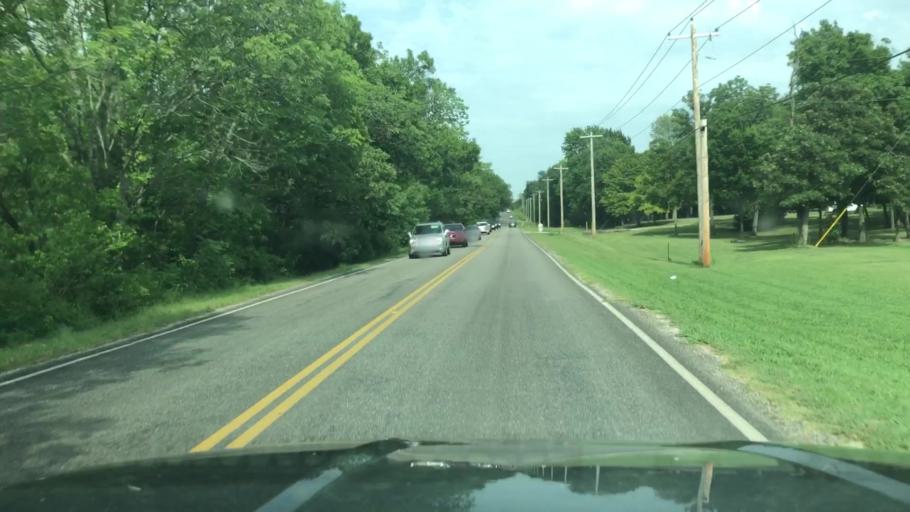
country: US
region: Oklahoma
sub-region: Tulsa County
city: Oakhurst
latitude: 36.0902
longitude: -96.1094
